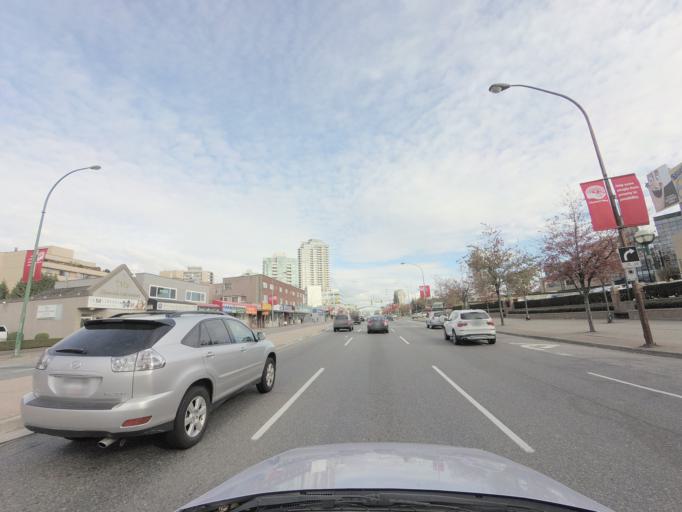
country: CA
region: British Columbia
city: Burnaby
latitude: 49.2288
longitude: -123.0005
